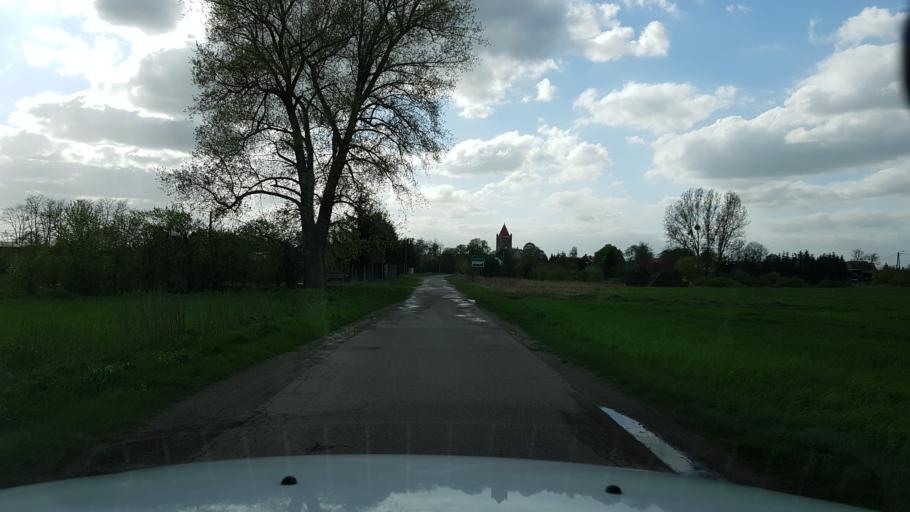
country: PL
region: West Pomeranian Voivodeship
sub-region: Powiat pyrzycki
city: Przelewice
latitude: 53.0223
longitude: 15.0840
